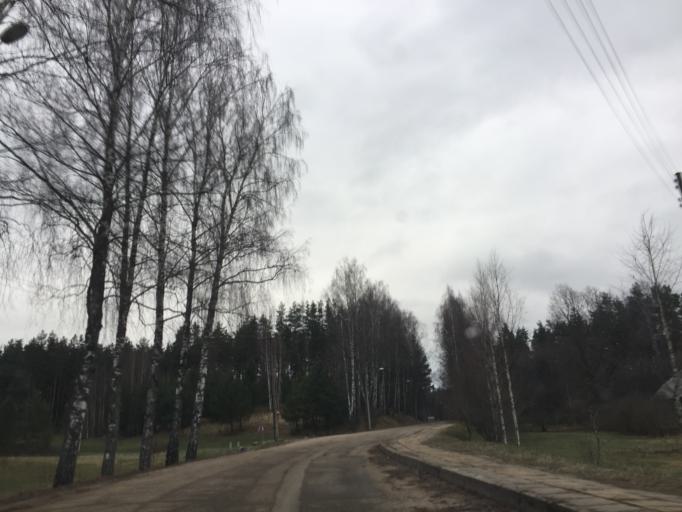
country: LV
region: Cesu Rajons
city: Cesis
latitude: 57.3237
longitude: 25.2574
